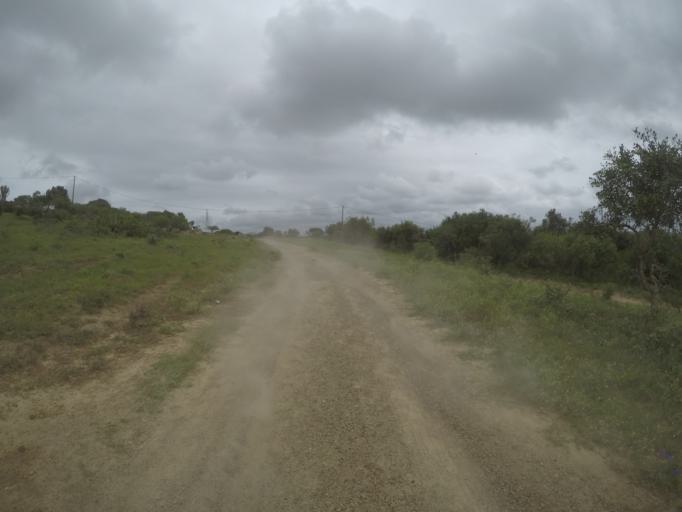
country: ZA
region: KwaZulu-Natal
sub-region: uThungulu District Municipality
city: Empangeni
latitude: -28.5994
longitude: 31.8484
